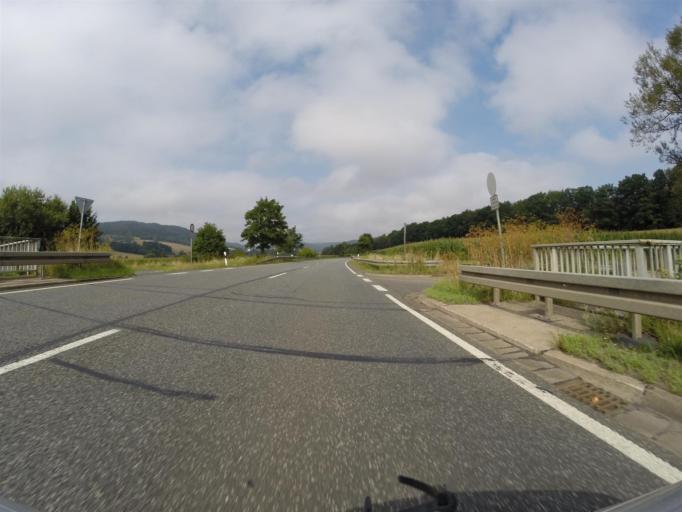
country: DE
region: Hesse
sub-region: Regierungsbezirk Kassel
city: Sontra
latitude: 51.1379
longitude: 9.9572
